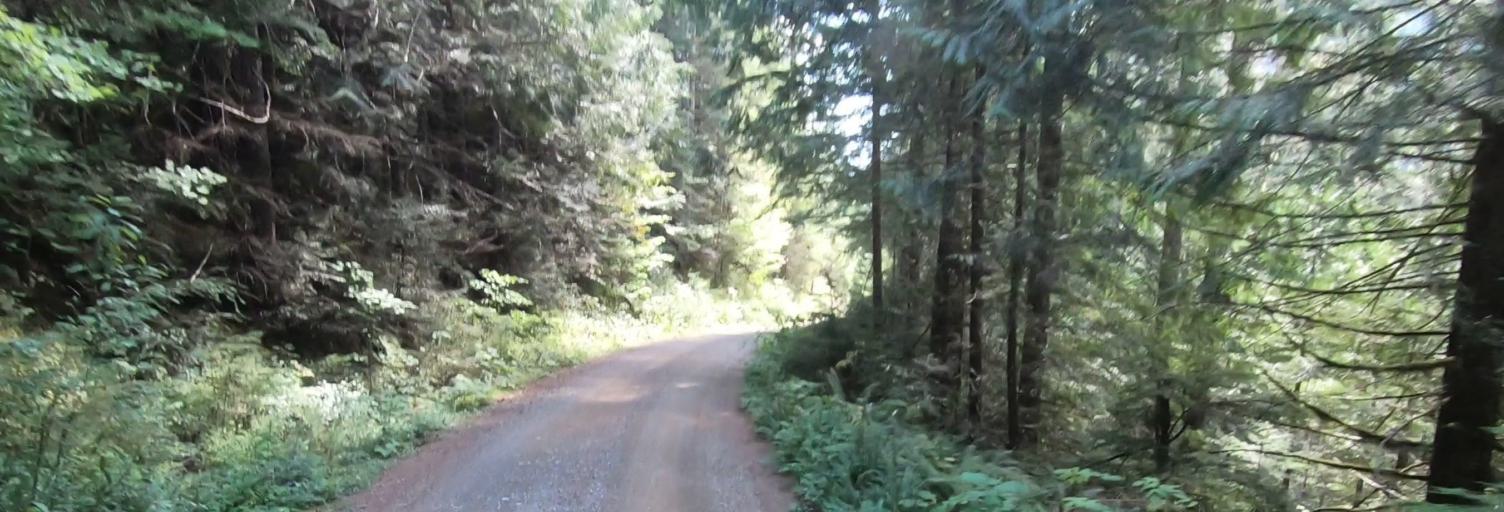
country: CA
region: British Columbia
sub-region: Fraser Valley Regional District
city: Chilliwack
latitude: 48.8955
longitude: -121.7973
